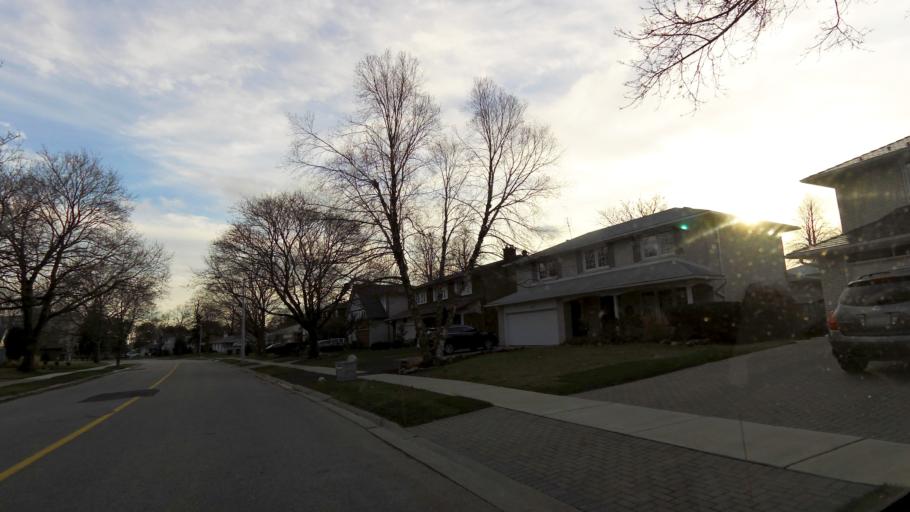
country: CA
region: Ontario
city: Etobicoke
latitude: 43.6315
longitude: -79.5825
